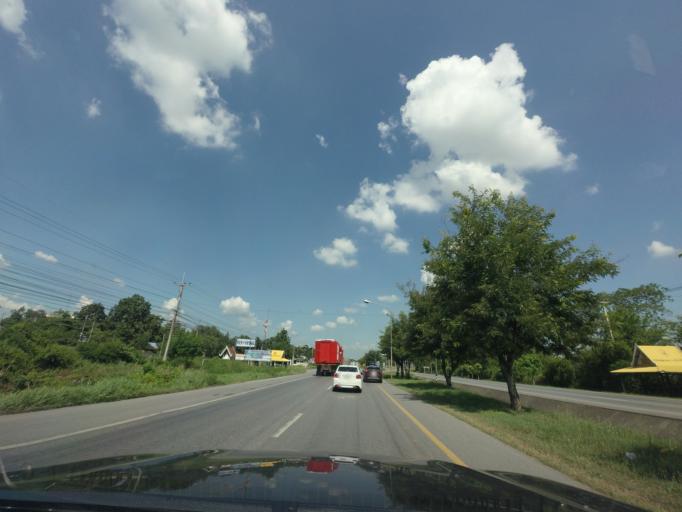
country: TH
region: Nakhon Ratchasima
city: Chaloem Phra Kiat
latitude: 15.0634
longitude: 102.1835
